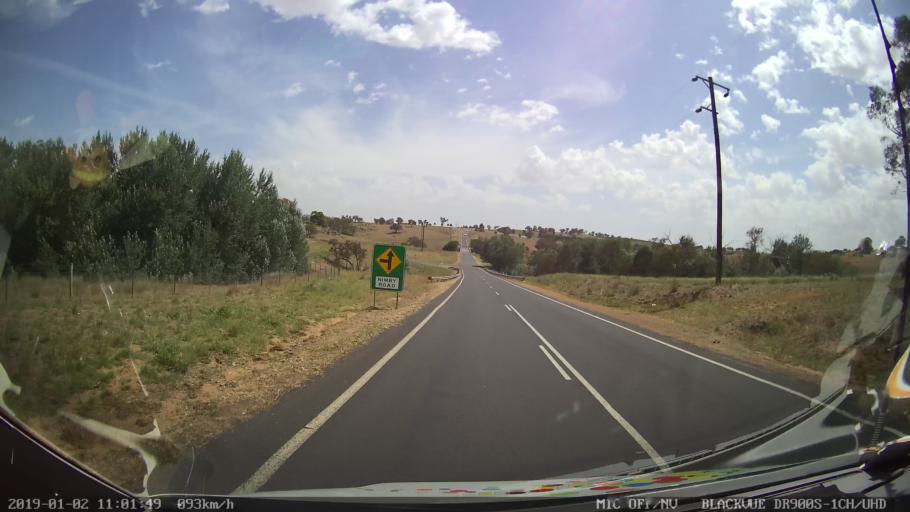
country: AU
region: New South Wales
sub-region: Young
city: Young
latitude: -34.5934
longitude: 148.3226
